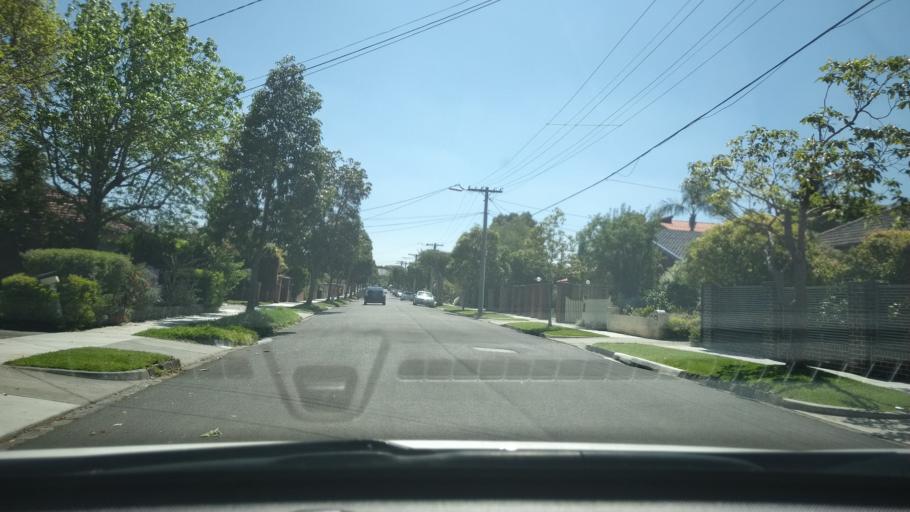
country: AU
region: Victoria
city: Ormond
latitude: -37.8910
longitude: 145.0338
